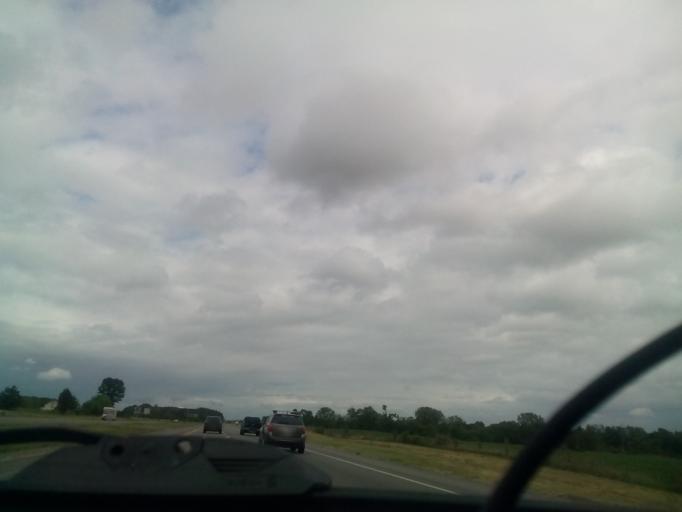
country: US
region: Ohio
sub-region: Williams County
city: Montpelier
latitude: 41.6276
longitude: -84.7225
